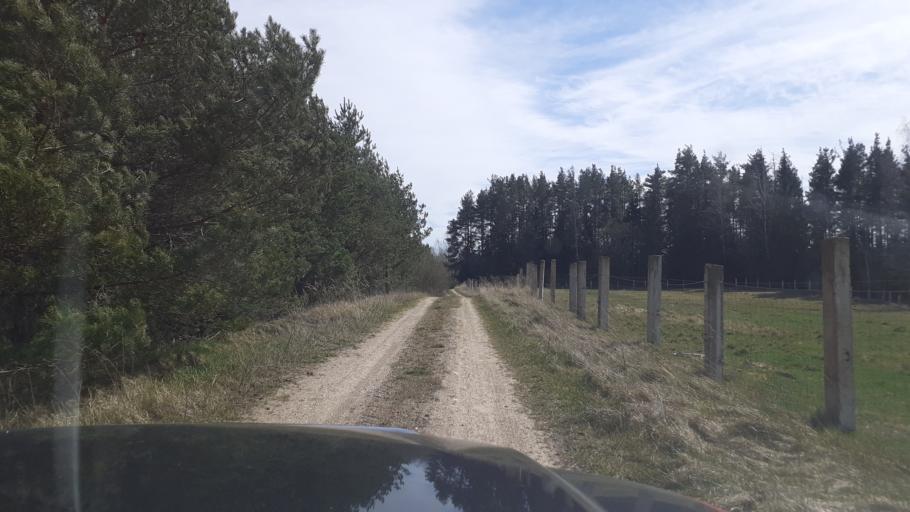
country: LV
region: Skrunda
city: Skrunda
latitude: 56.8292
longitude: 22.0150
